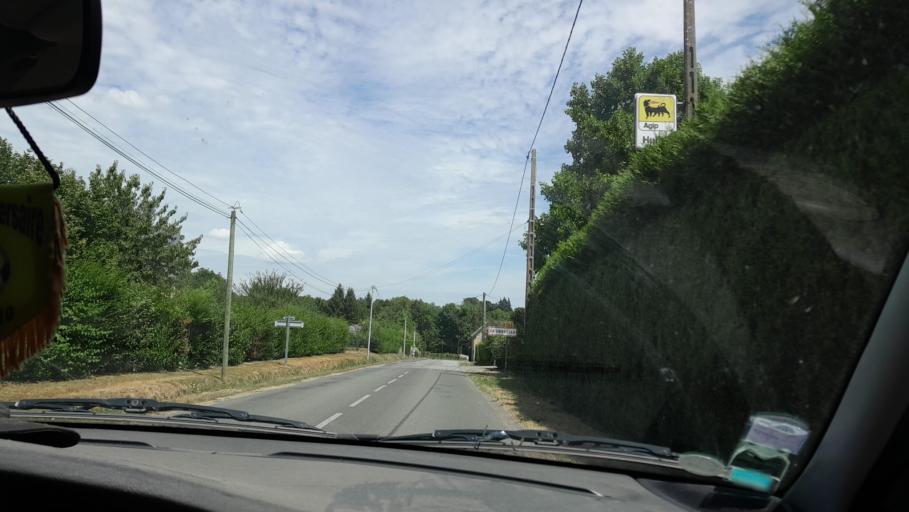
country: FR
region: Brittany
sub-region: Departement d'Ille-et-Vilaine
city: Le Pertre
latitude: 48.0684
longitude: -1.0213
